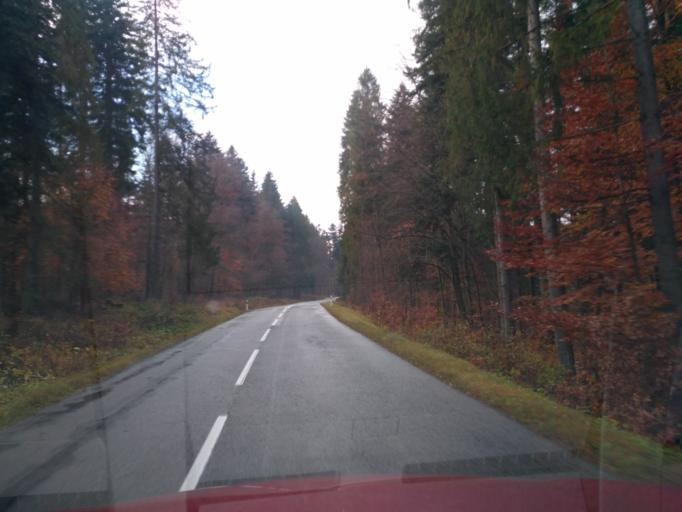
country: SK
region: Kosicky
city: Medzev
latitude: 48.7908
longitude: 20.7553
